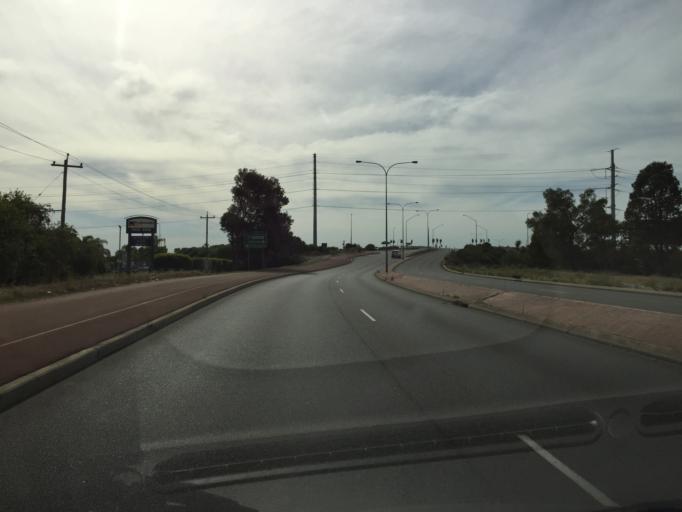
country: AU
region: Western Australia
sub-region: Canning
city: Canning Vale
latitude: -32.0594
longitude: 115.9062
